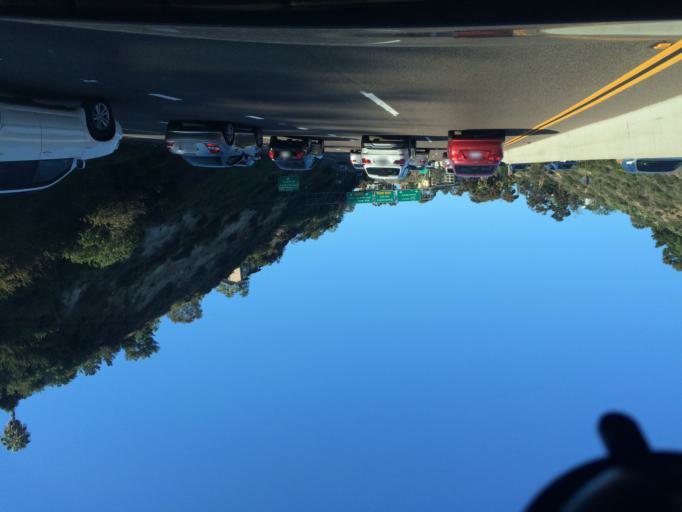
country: US
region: California
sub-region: San Diego County
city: San Diego
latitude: 32.7563
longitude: -117.1591
